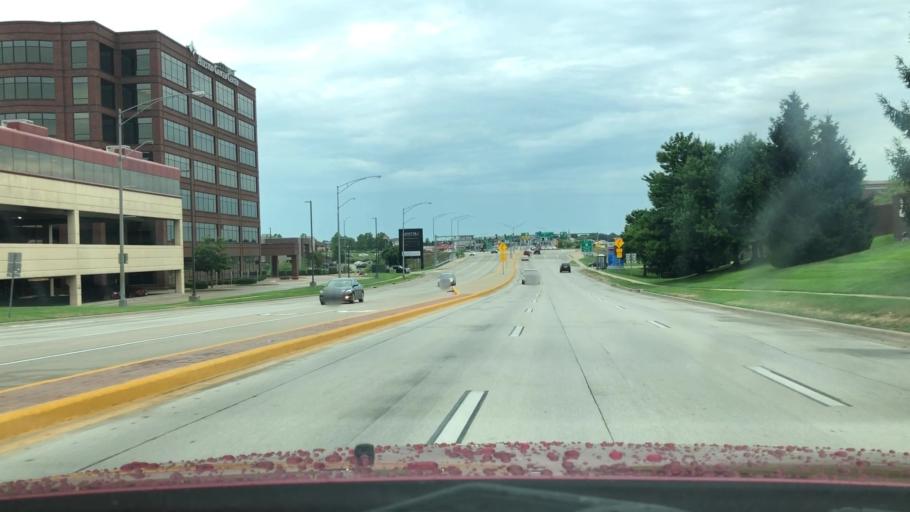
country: US
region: Missouri
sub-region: Greene County
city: Springfield
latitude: 37.1460
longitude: -93.2780
